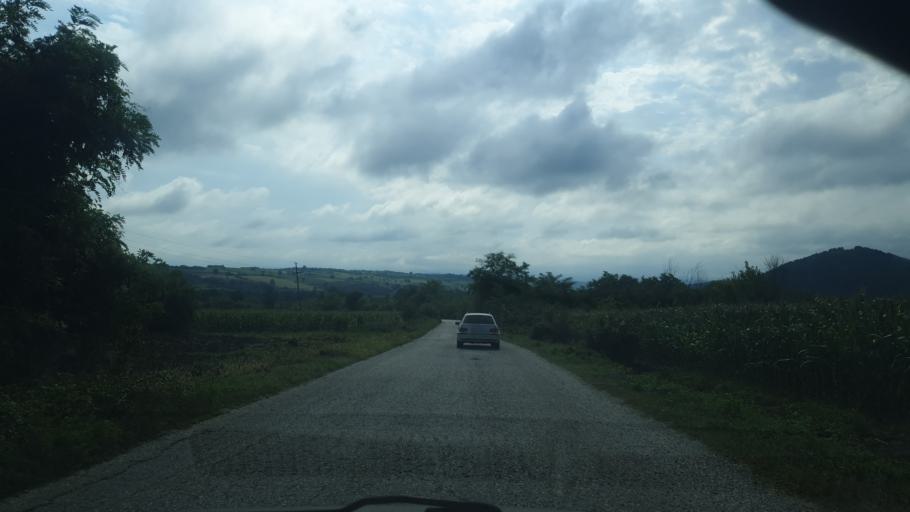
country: RS
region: Central Serbia
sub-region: Sumadijski Okrug
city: Kragujevac
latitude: 44.0963
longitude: 20.7864
